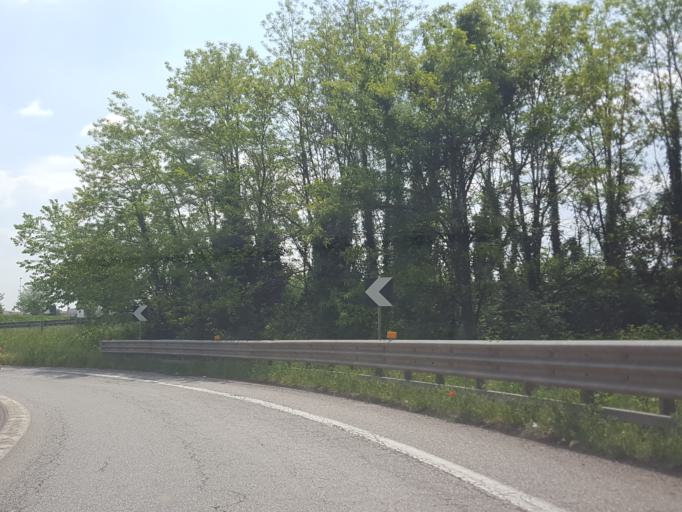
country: IT
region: Veneto
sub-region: Provincia di Verona
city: Poiano
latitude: 45.4624
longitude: 11.0173
